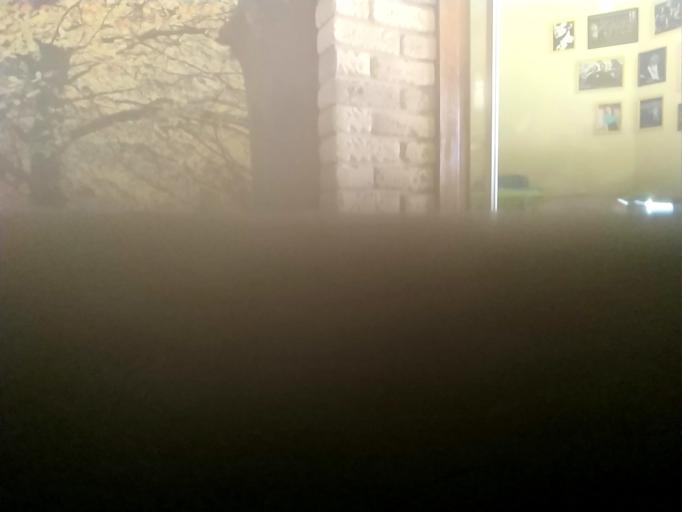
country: RU
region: Kaluga
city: Yukhnov
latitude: 54.8091
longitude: 35.0101
